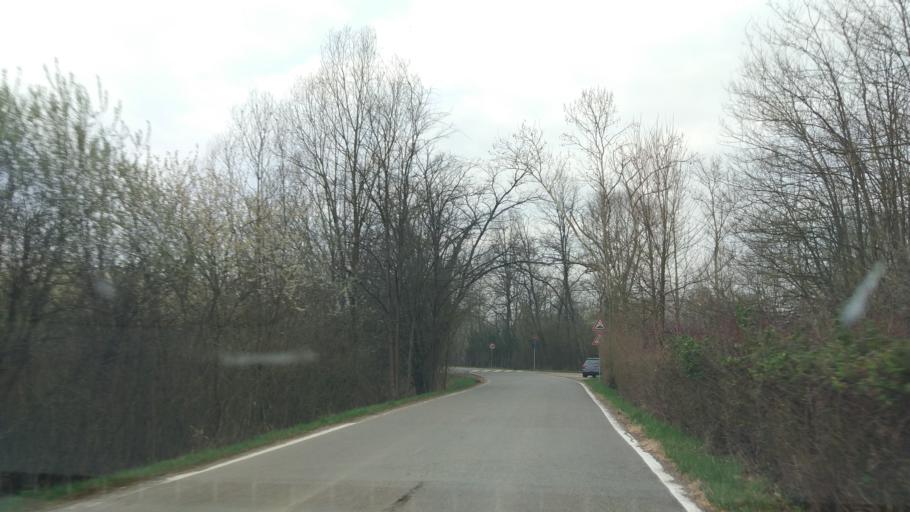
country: IT
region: Lombardy
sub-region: Provincia di Monza e Brianza
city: Capriano
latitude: 45.7358
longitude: 9.2449
